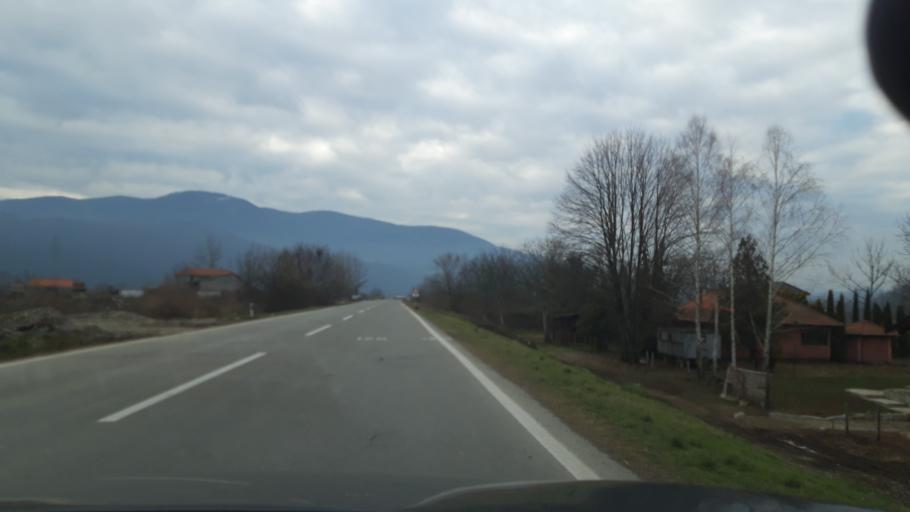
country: RS
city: Trsic
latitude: 44.5323
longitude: 19.1808
